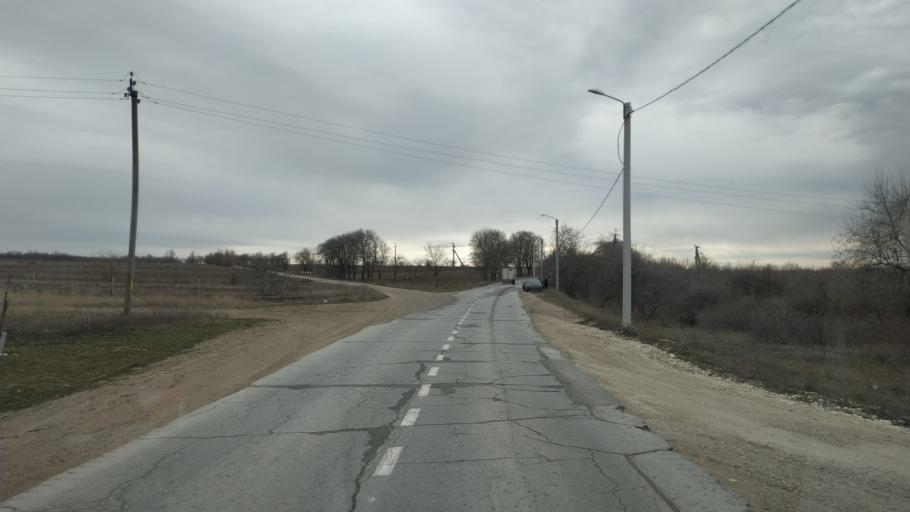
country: MD
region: Telenesti
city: Cocieri
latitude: 47.3369
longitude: 29.0980
